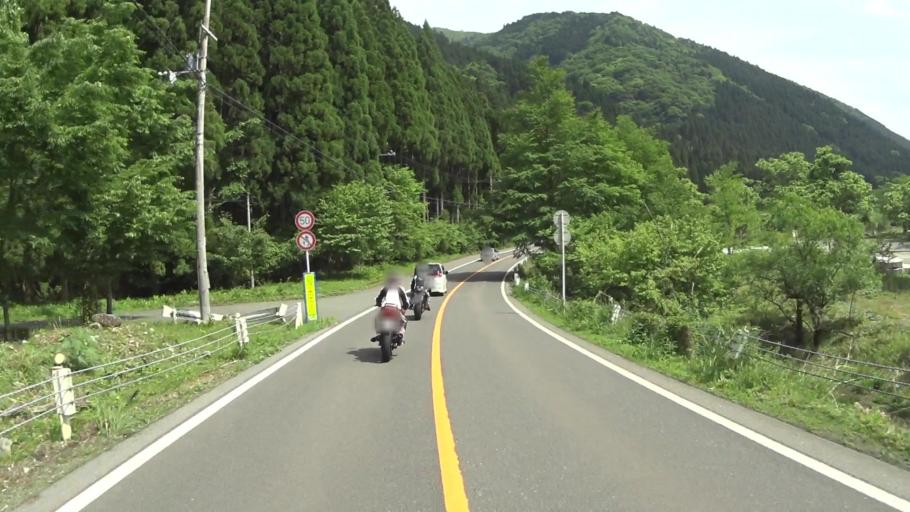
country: JP
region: Shiga Prefecture
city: Kitahama
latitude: 35.2889
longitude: 135.8841
